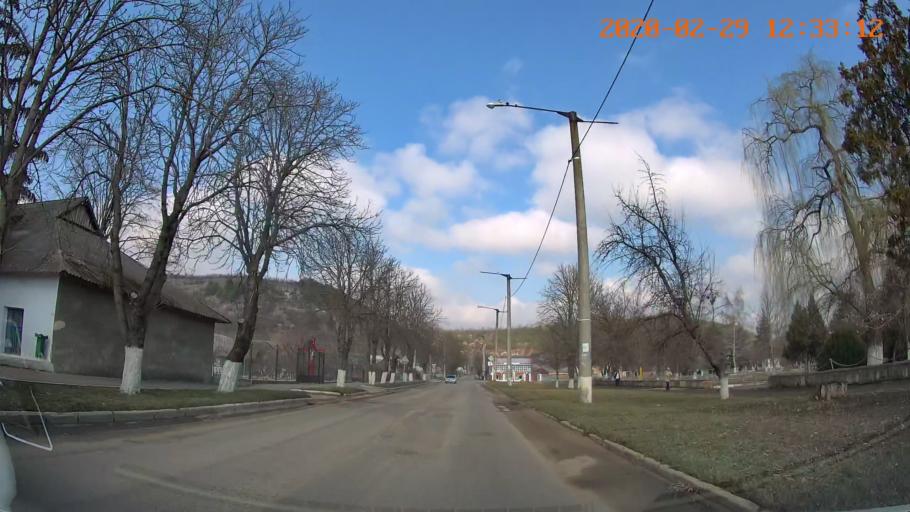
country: MD
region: Telenesti
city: Camenca
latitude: 48.0339
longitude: 28.7034
